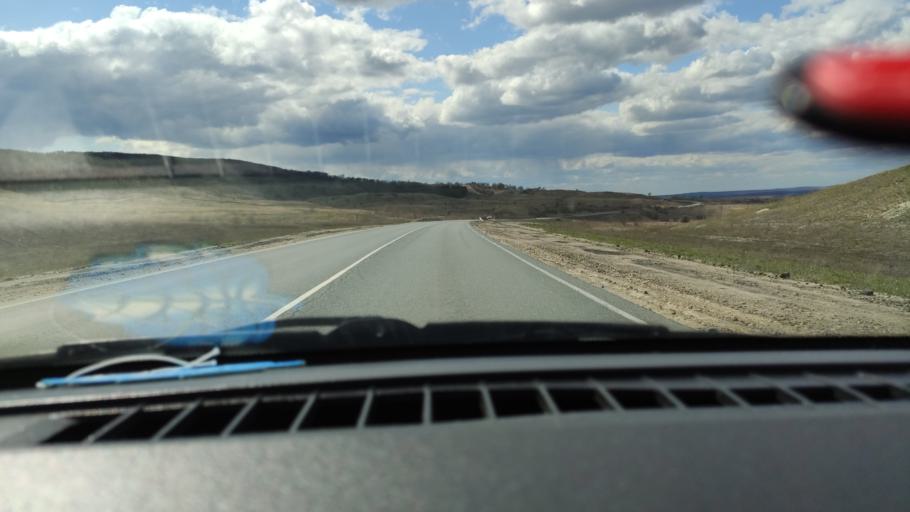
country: RU
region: Saratov
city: Alekseyevka
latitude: 52.3359
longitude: 47.9299
